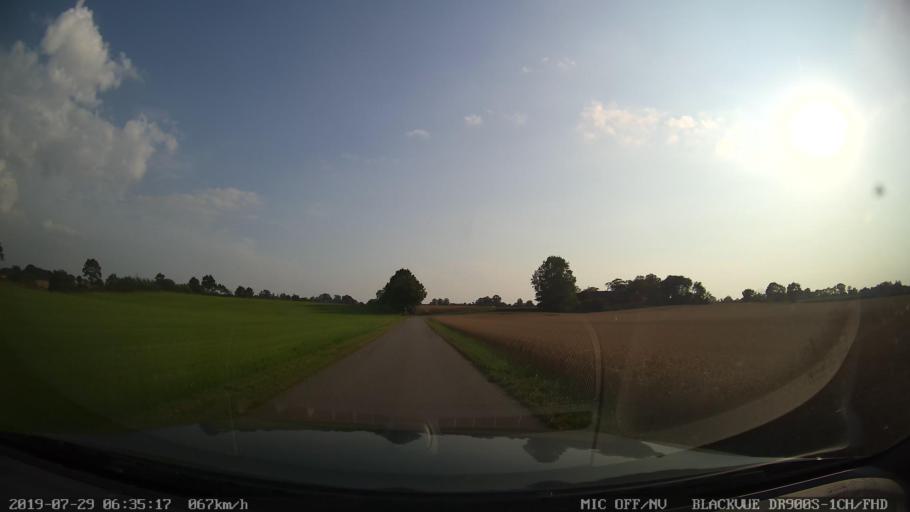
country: SE
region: Skane
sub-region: Helsingborg
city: Odakra
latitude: 56.1140
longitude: 12.7191
